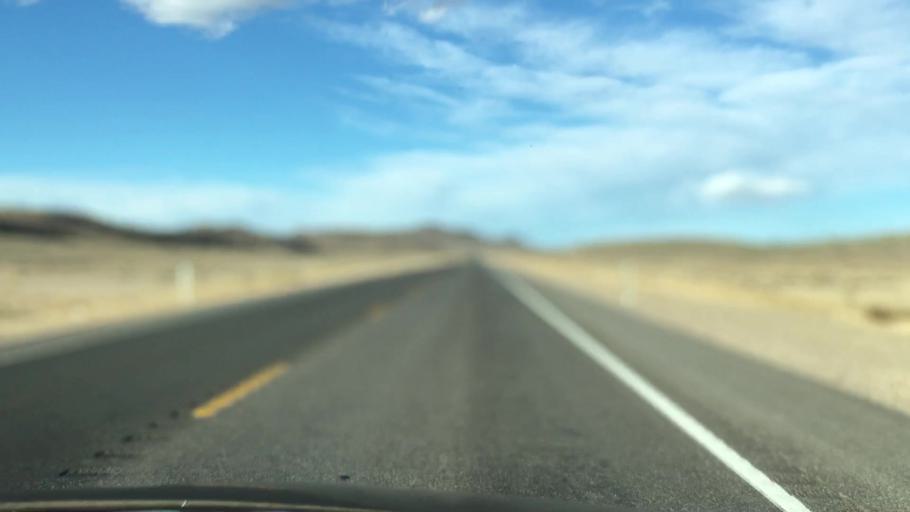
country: US
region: Nevada
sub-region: Esmeralda County
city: Goldfield
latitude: 37.6310
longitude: -117.2183
